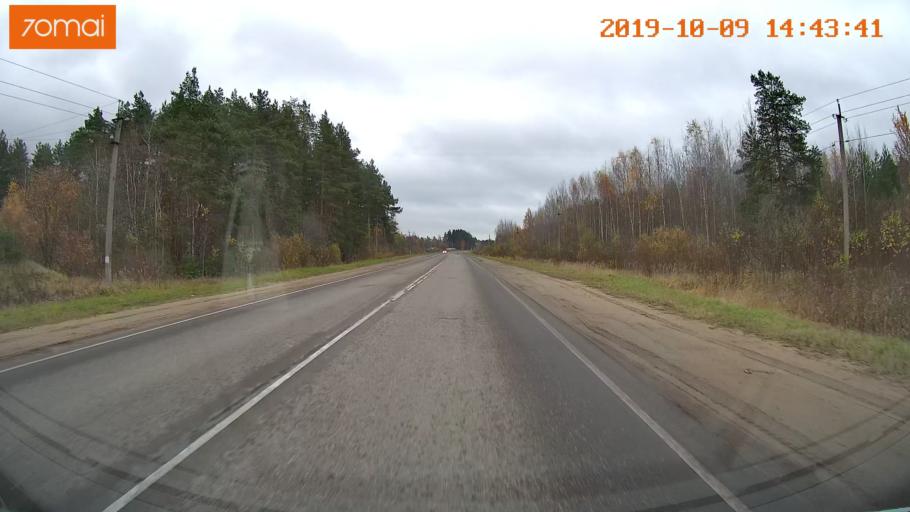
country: RU
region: Kostroma
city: Buy
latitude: 58.4566
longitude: 41.5493
